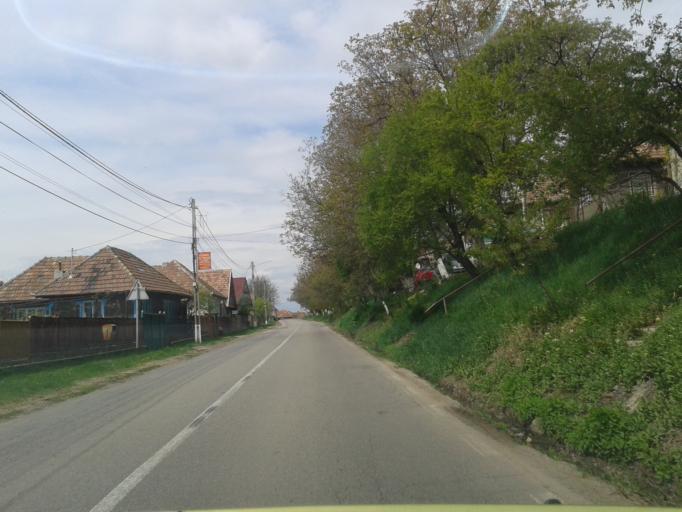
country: RO
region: Alba
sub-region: Comuna Valea Lunga
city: Valea Lunga
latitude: 46.1220
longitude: 24.0322
